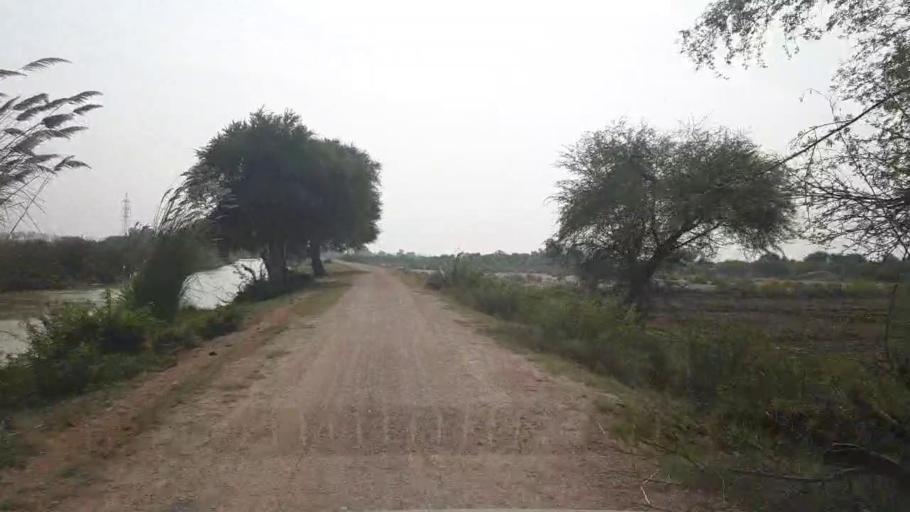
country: PK
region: Sindh
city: Tando Muhammad Khan
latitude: 25.1282
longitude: 68.4353
